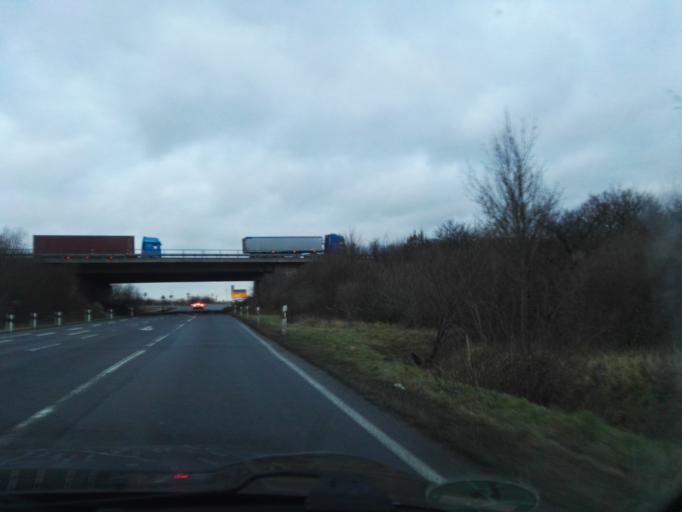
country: DE
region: Lower Saxony
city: Leiferde
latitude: 52.1967
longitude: 10.4569
